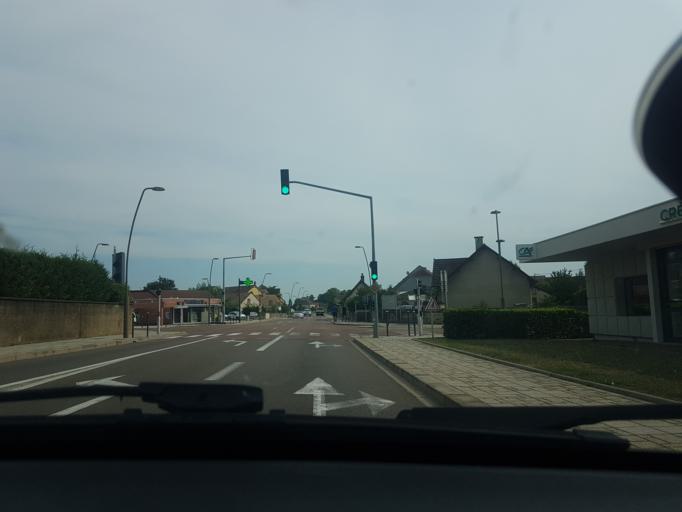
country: FR
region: Bourgogne
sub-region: Departement de Saone-et-Loire
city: Saint-Marcel
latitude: 46.7733
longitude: 4.8929
